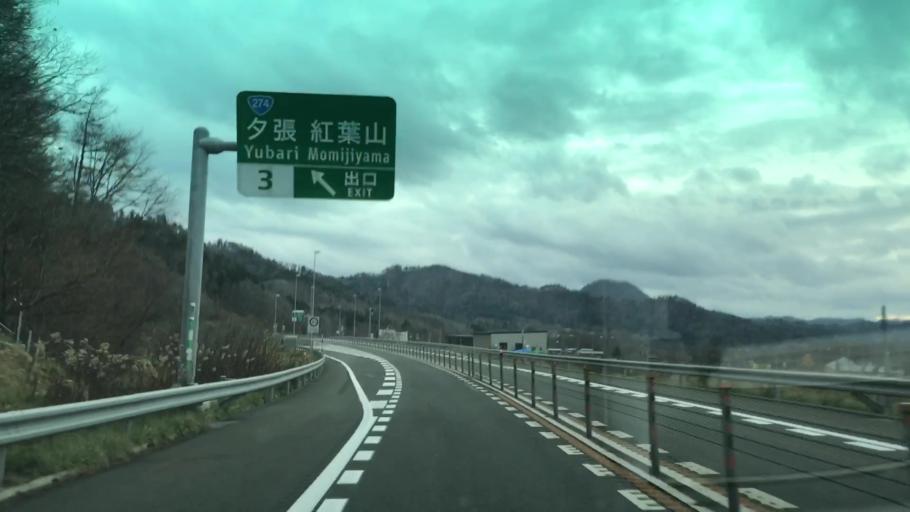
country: JP
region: Hokkaido
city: Iwamizawa
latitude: 42.9268
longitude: 142.0363
